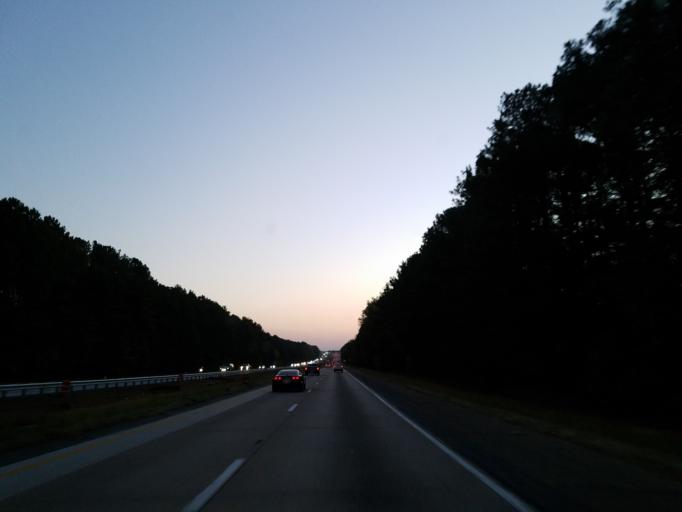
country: US
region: Georgia
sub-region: Fulton County
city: Milton
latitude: 34.1288
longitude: -84.2114
